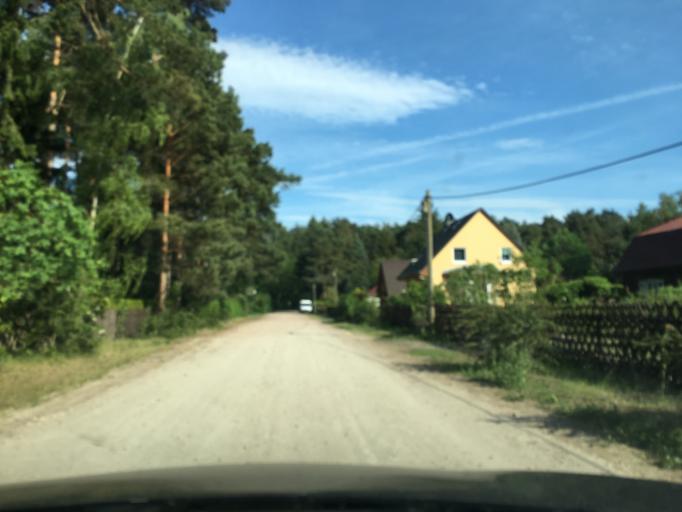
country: DE
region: Brandenburg
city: Grunheide
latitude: 52.4460
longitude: 13.8640
